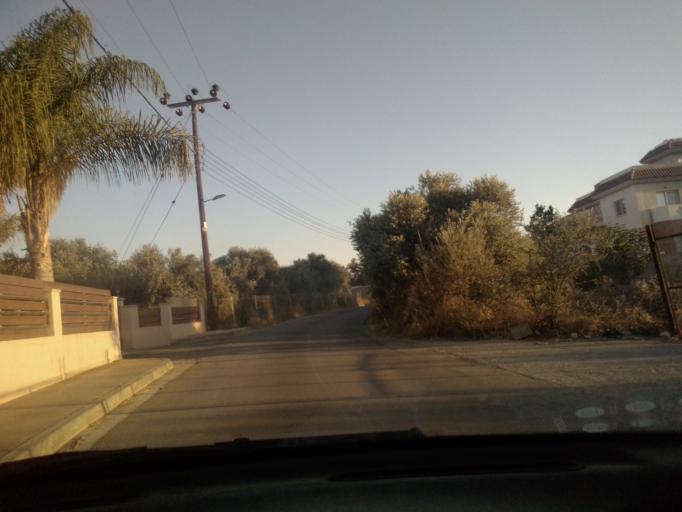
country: CY
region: Limassol
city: Ypsonas
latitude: 34.6767
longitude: 32.9622
